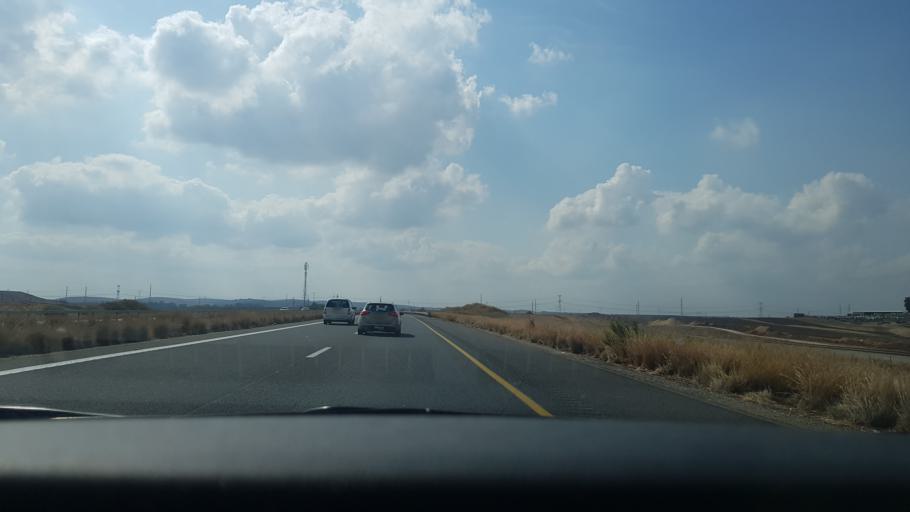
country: IL
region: Central District
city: Bene 'Ayish
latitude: 31.7248
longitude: 34.8206
